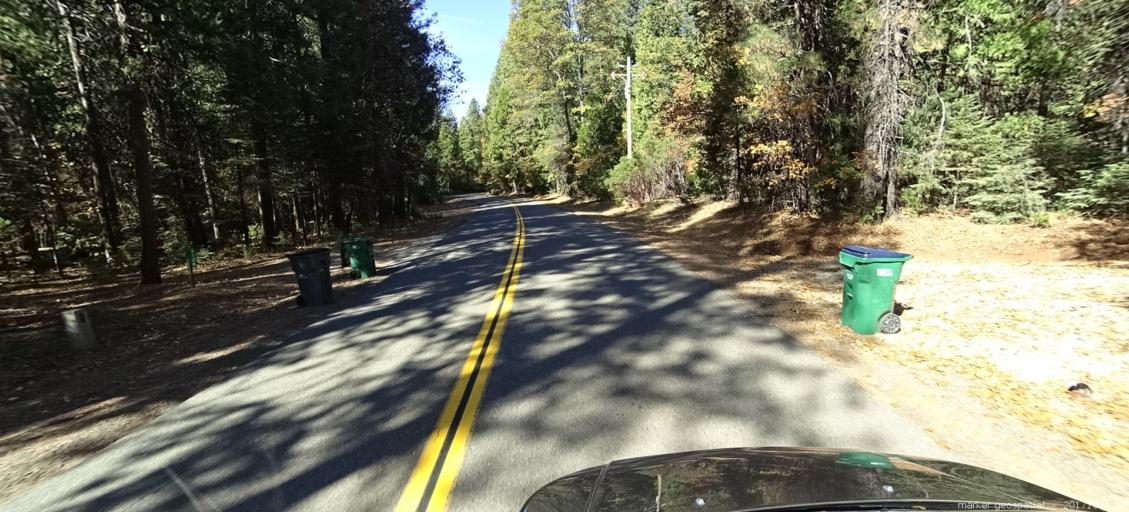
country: US
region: California
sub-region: Shasta County
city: Shingletown
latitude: 40.4866
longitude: -121.8825
